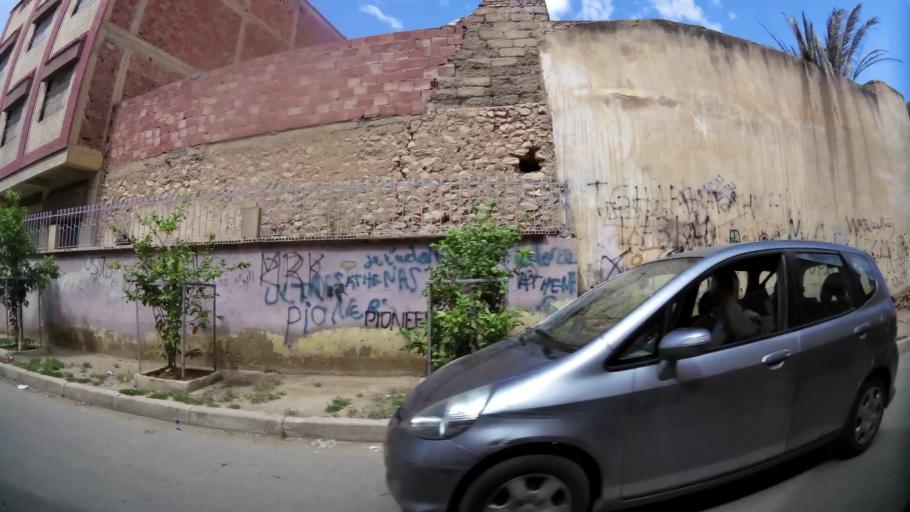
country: MA
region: Oriental
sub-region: Oujda-Angad
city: Oujda
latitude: 34.6844
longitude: -1.9049
